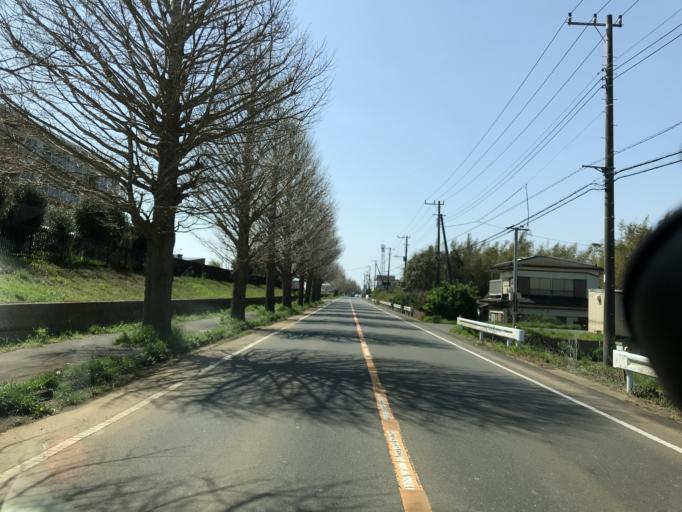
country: JP
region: Chiba
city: Asahi
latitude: 35.7903
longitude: 140.7067
